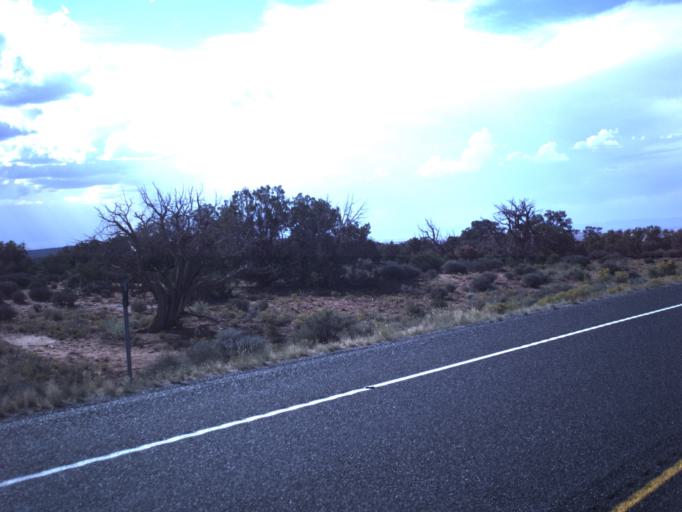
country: US
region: Utah
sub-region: Grand County
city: Moab
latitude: 38.5873
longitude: -109.8061
